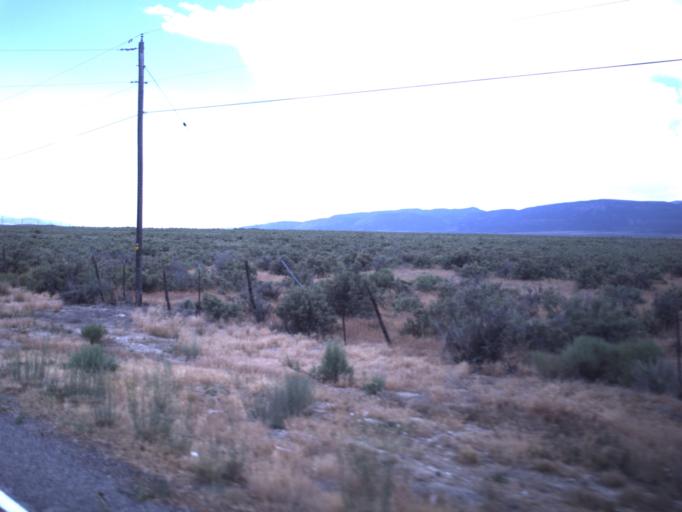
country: US
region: Utah
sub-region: Sanpete County
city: Moroni
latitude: 39.4451
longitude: -111.5625
